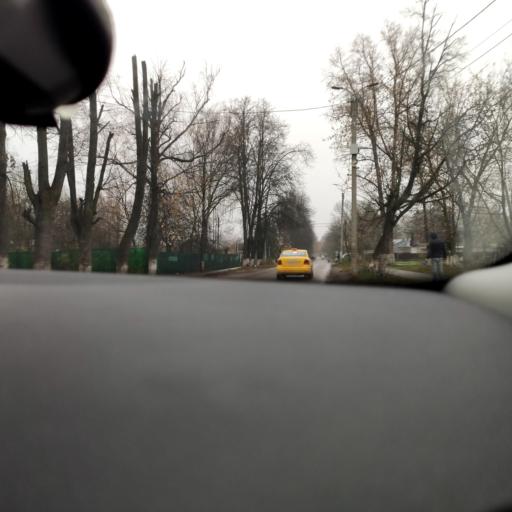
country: RU
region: Moskovskaya
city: Dedovsk
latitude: 55.8615
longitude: 37.1286
